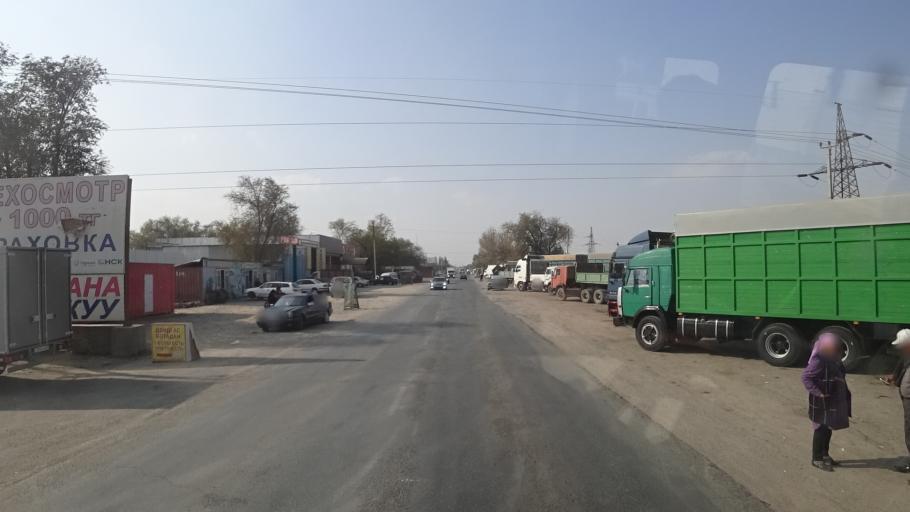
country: KZ
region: Zhambyl
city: Taraz
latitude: 42.9236
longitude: 71.4227
